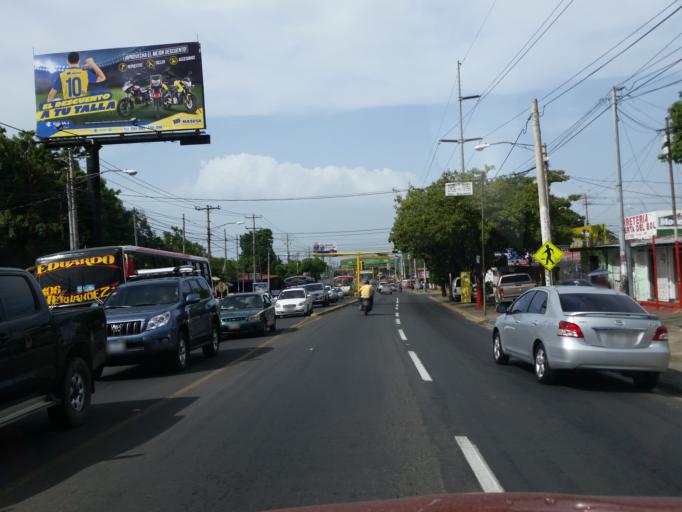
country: NI
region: Managua
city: Managua
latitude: 12.1152
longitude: -86.2533
